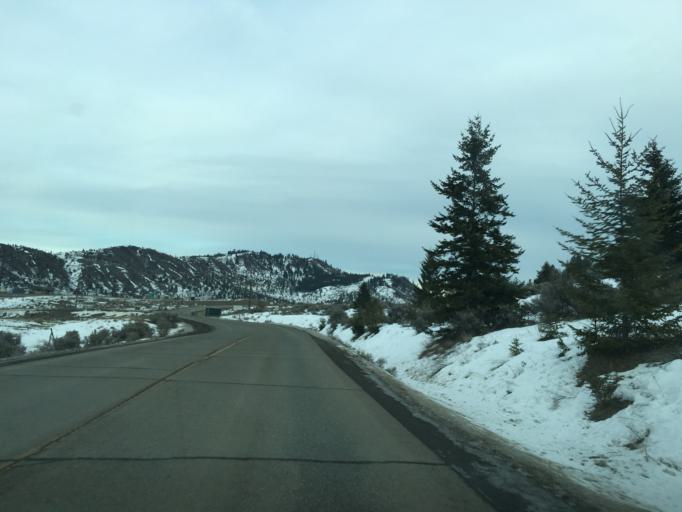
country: CA
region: British Columbia
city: Kamloops
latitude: 50.6638
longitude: -120.4306
